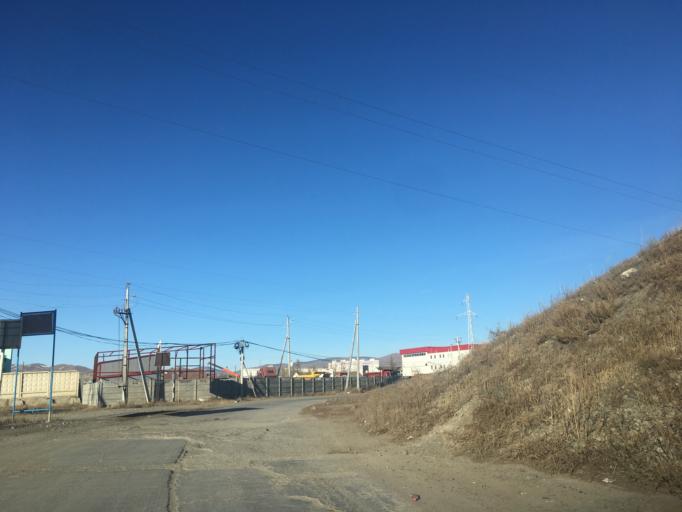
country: MN
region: Ulaanbaatar
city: Ulaanbaatar
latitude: 47.9010
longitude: 106.7969
